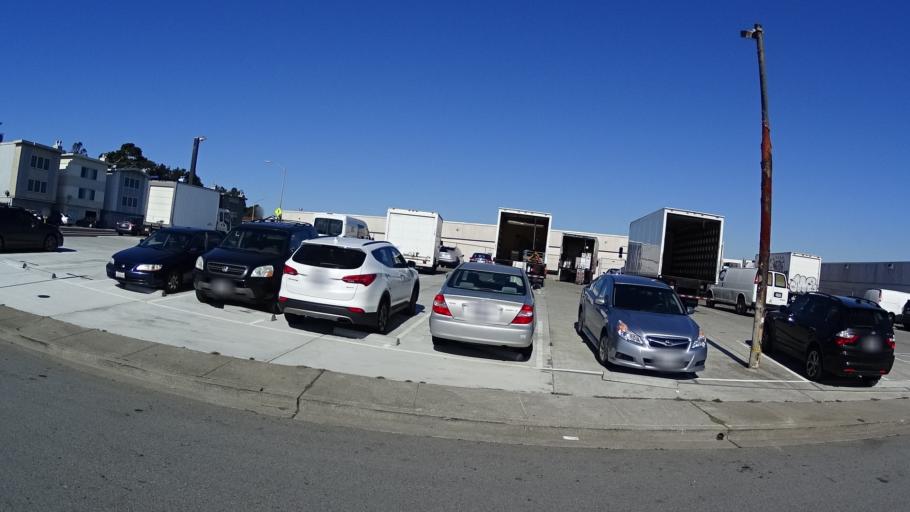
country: US
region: California
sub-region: San Mateo County
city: Colma
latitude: 37.6505
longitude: -122.4687
